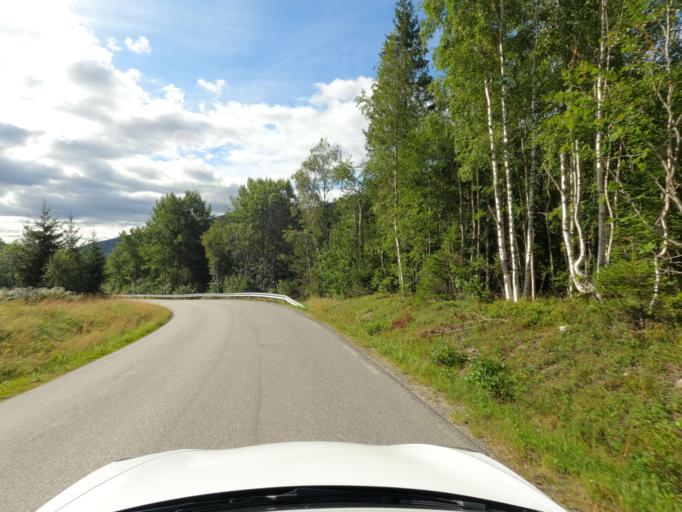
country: NO
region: Buskerud
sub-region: Nore og Uvdal
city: Rodberg
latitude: 60.0759
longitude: 8.7701
